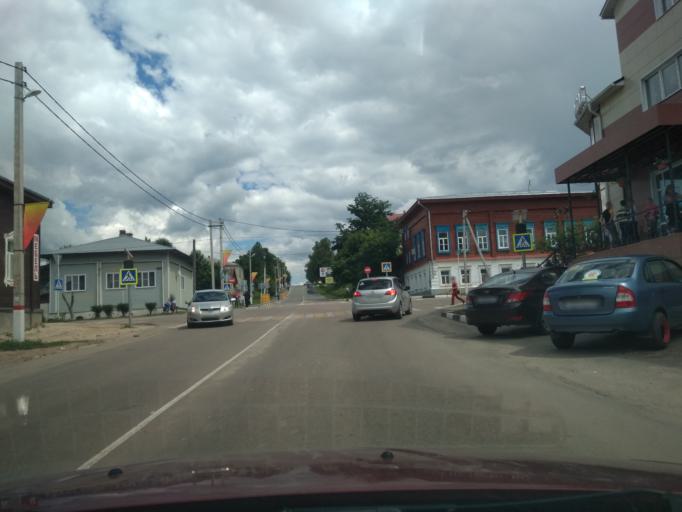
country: RU
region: Vladimir
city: Melenki
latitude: 55.3383
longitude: 41.6263
